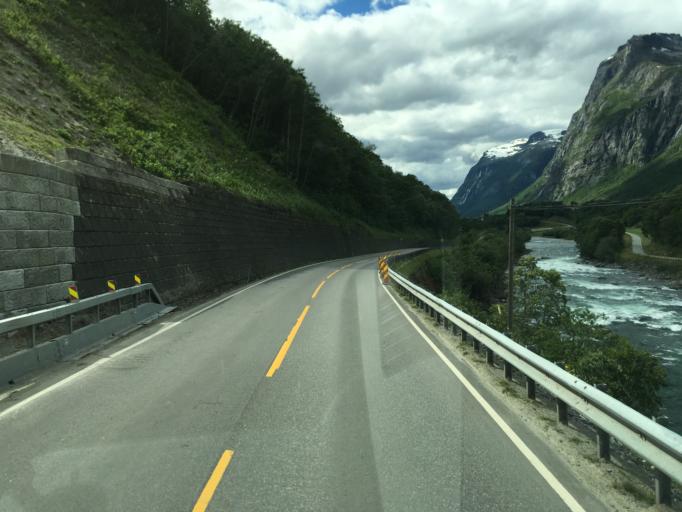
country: NO
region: More og Romsdal
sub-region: Sunndal
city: Sunndalsora
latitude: 62.6325
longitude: 8.8400
